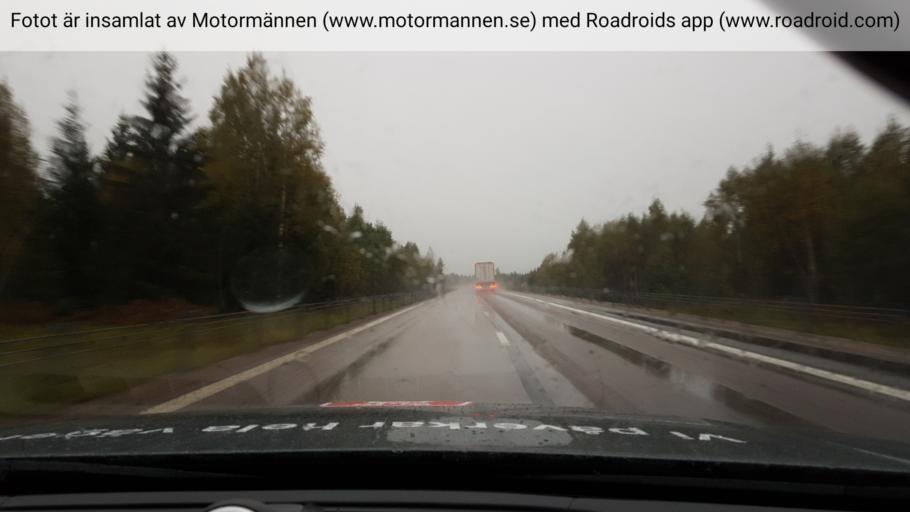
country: SE
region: Uppsala
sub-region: Tierps Kommun
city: Tierp
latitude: 60.3953
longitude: 17.4753
